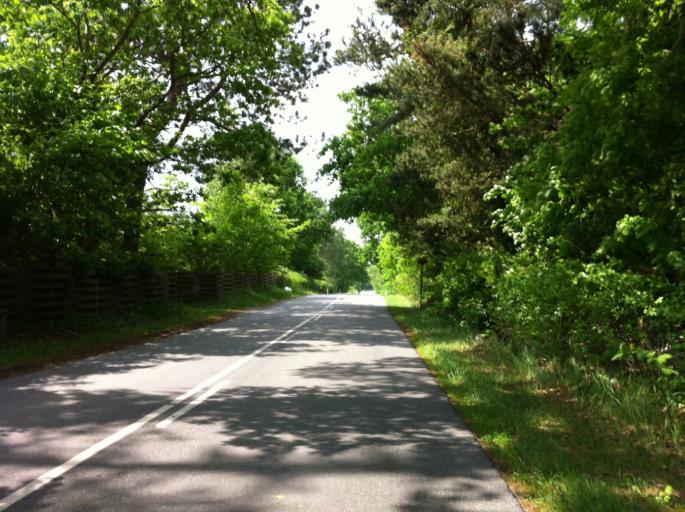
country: DK
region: Capital Region
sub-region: Gribskov Kommune
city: Helsinge
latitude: 56.1101
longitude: 12.1992
